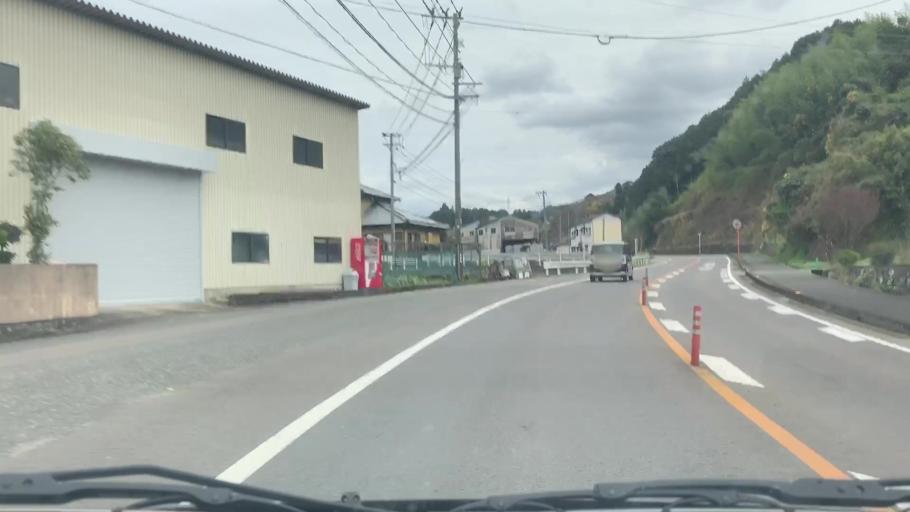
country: JP
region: Saga Prefecture
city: Ureshinomachi-shimojuku
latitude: 33.1001
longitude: 130.0006
